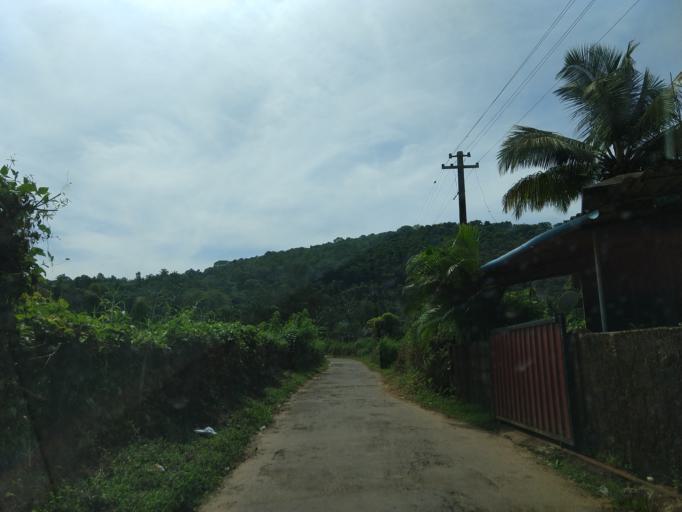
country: IN
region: Maharashtra
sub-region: Sindhudurg
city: Savantvadi
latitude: 15.9735
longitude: 73.7874
